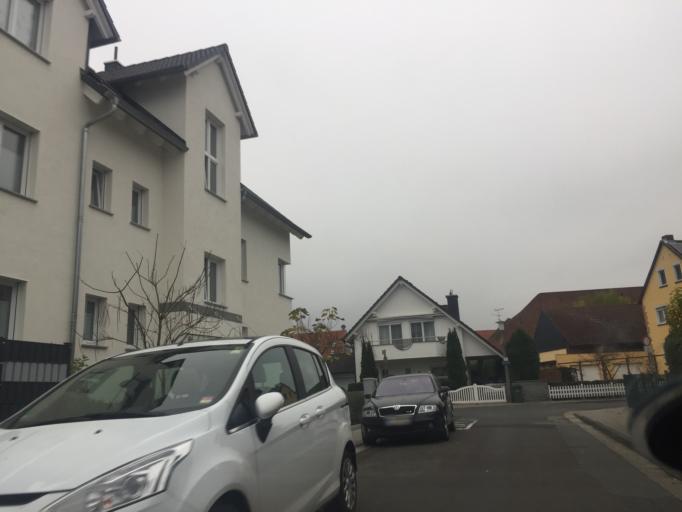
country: DE
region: Hesse
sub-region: Regierungsbezirk Darmstadt
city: Maintal
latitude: 50.1516
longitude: 8.8302
